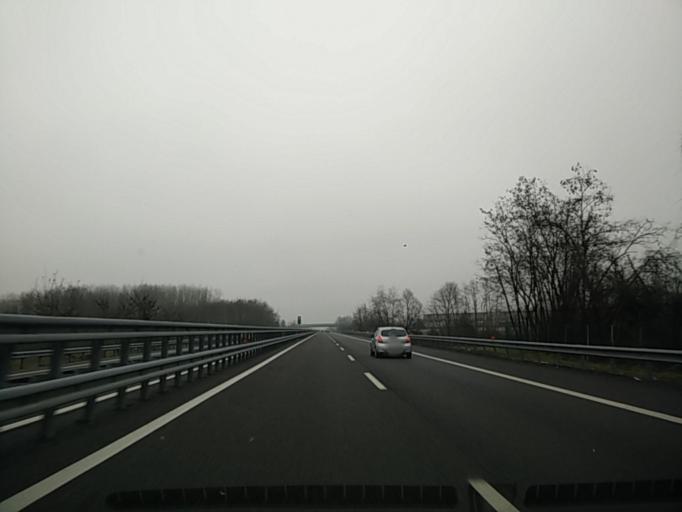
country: IT
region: Piedmont
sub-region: Provincia di Asti
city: Villafranca d'Asti
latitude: 44.9255
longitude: 8.0148
